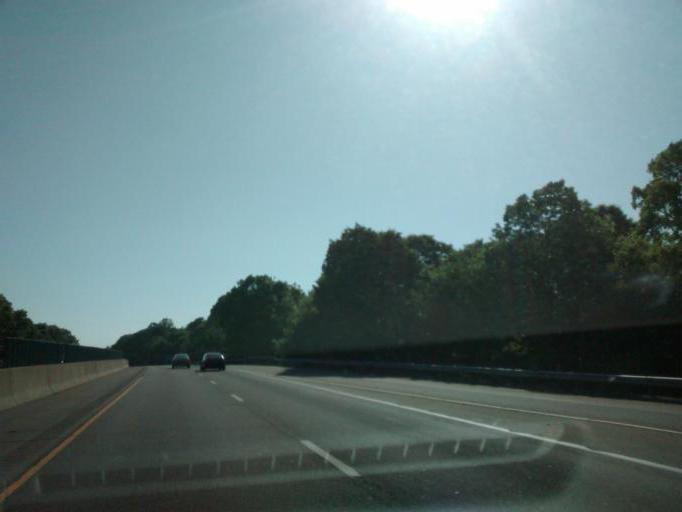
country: US
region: Connecticut
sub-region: Middlesex County
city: Old Saybrook
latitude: 41.3047
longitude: -72.3813
